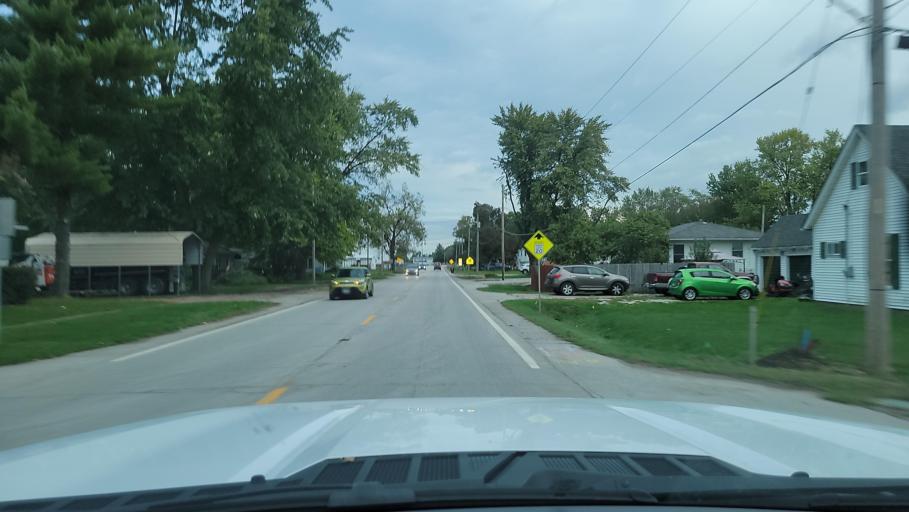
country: US
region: Illinois
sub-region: Schuyler County
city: Rushville
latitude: 40.1255
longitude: -90.5635
